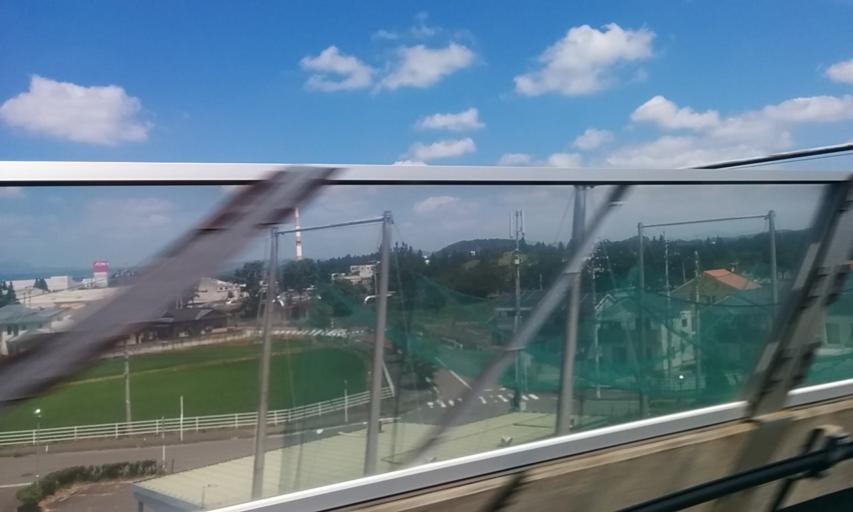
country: JP
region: Tochigi
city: Kuroiso
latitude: 37.1175
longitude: 140.1836
